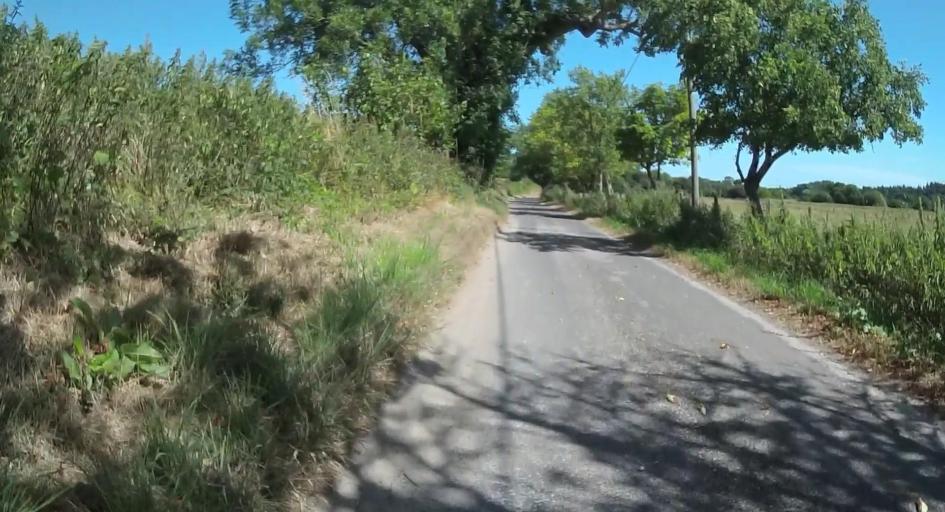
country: GB
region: England
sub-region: Dorset
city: Bovington Camp
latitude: 50.7397
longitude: -2.2400
